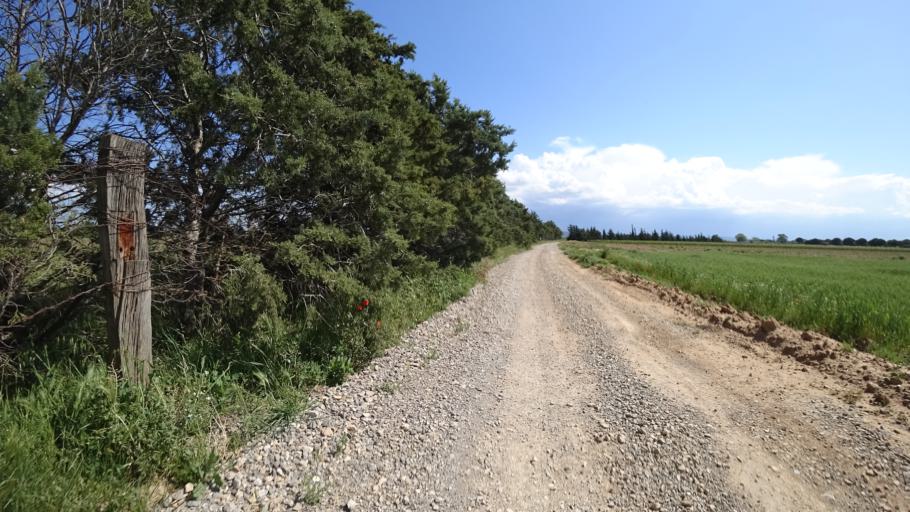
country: FR
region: Languedoc-Roussillon
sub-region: Departement de l'Aude
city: Ginestas
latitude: 43.2635
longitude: 2.8944
